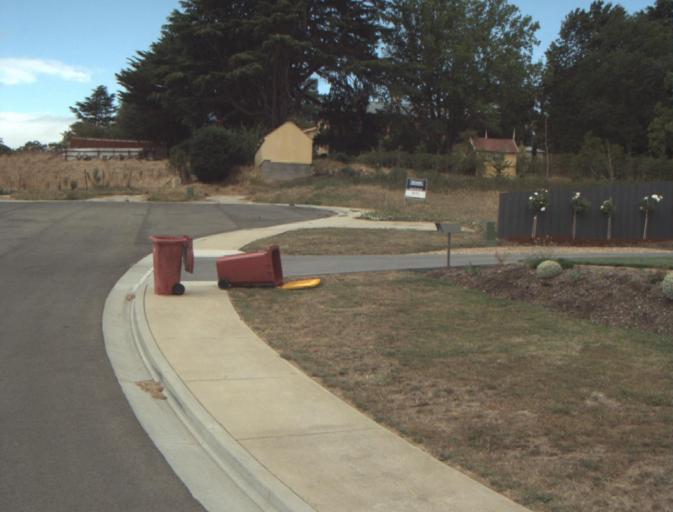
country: AU
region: Tasmania
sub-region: Launceston
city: Newstead
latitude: -41.4561
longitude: 147.2010
